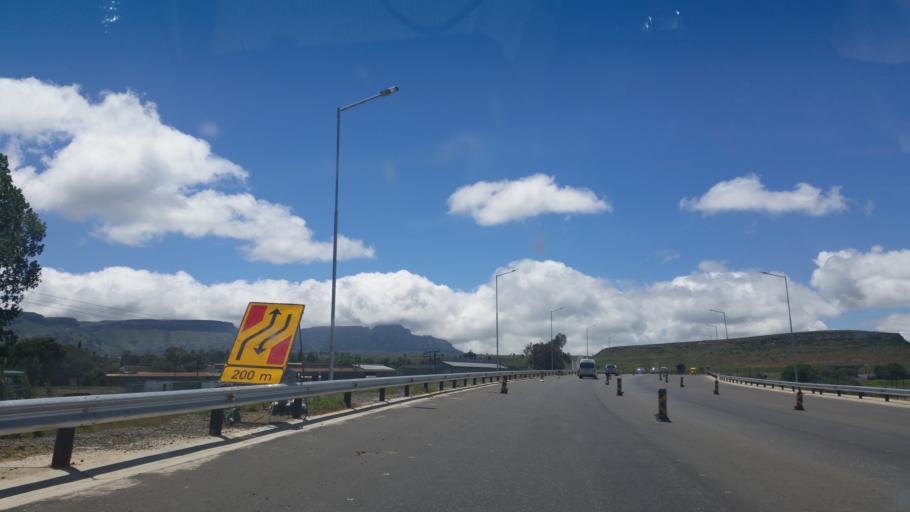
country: ZA
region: Orange Free State
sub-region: Thabo Mofutsanyana District Municipality
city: Harrismith
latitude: -28.2819
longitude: 29.1256
